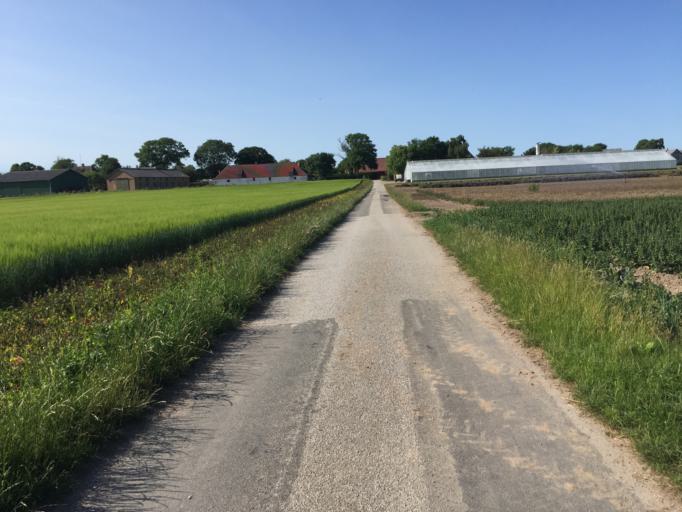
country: DK
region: Zealand
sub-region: Slagelse Kommune
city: Skaelskor
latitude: 55.2088
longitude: 11.1918
